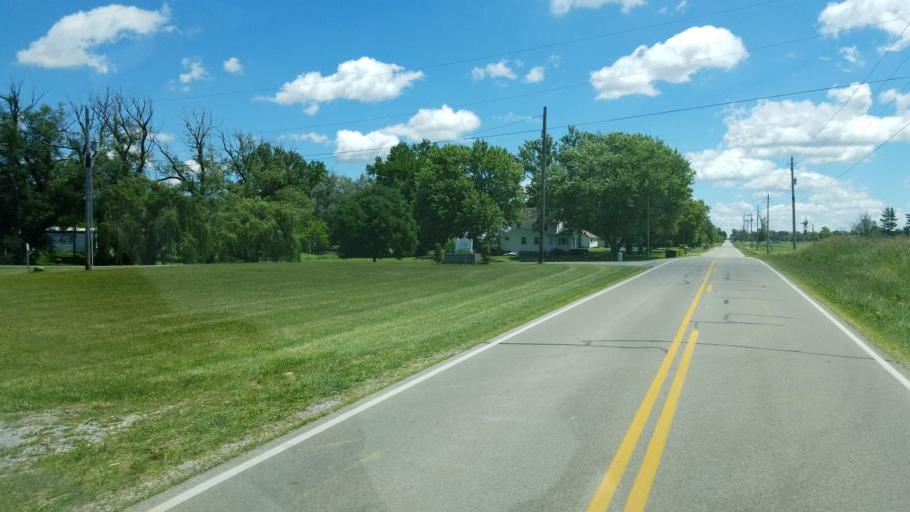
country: US
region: Ohio
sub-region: Crawford County
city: Galion
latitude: 40.7343
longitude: -82.8328
